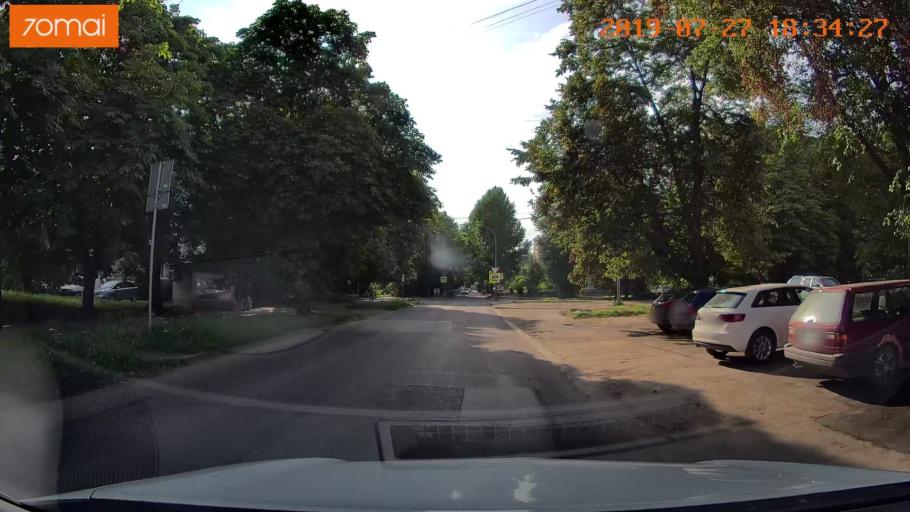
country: RU
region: Kaliningrad
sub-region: Gorod Kaliningrad
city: Kaliningrad
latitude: 54.7026
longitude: 20.5035
